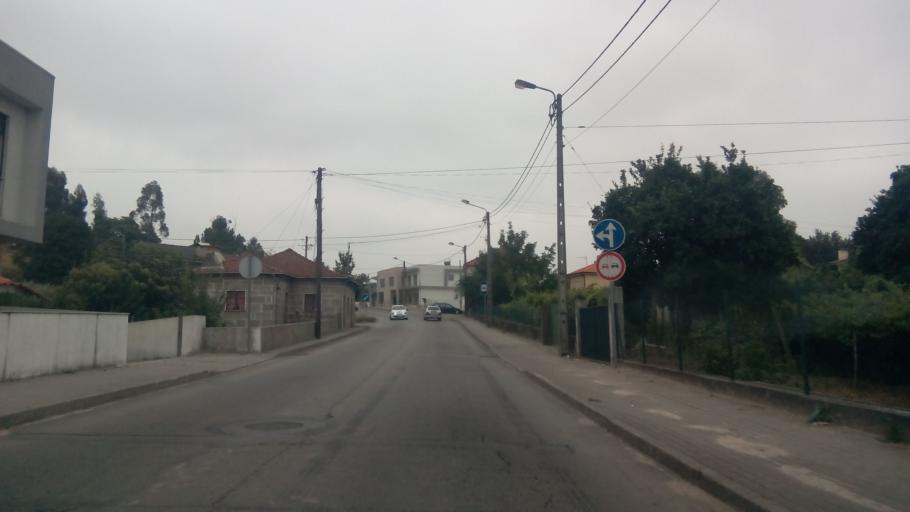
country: PT
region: Porto
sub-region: Paredes
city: Madalena
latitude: 41.2122
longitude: -8.3439
